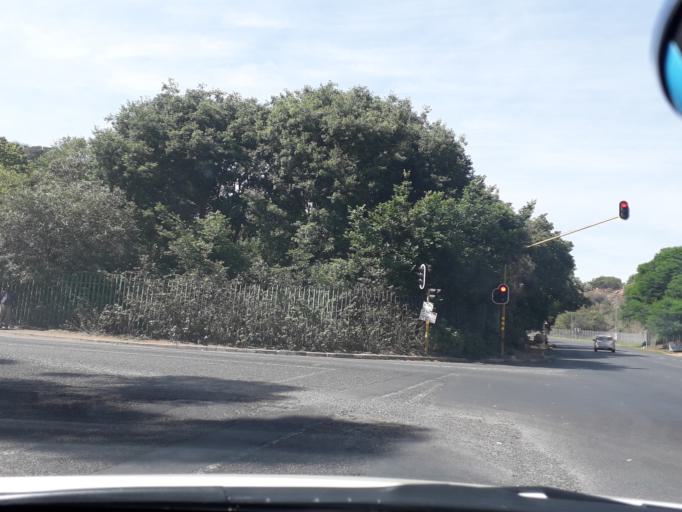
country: ZA
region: Gauteng
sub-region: City of Johannesburg Metropolitan Municipality
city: Johannesburg
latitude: -26.1675
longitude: 27.9986
